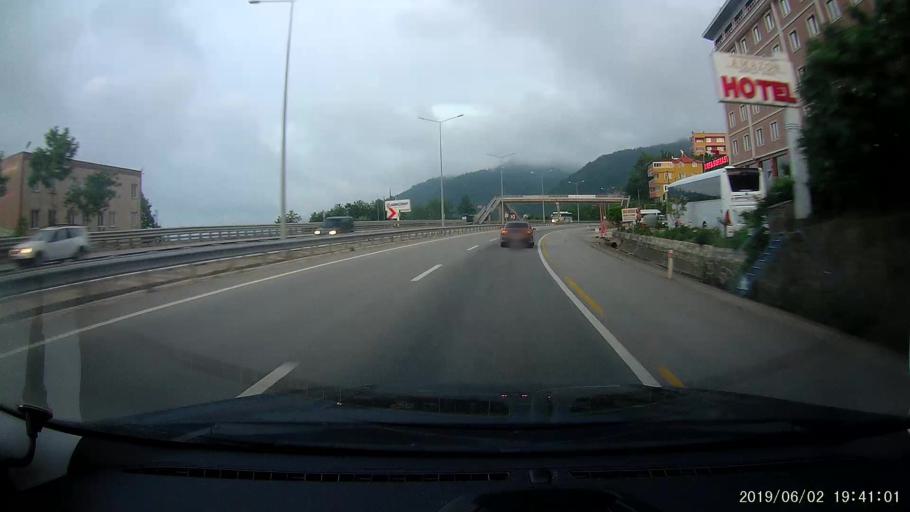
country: TR
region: Giresun
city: Kesap
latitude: 40.9177
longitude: 38.4723
